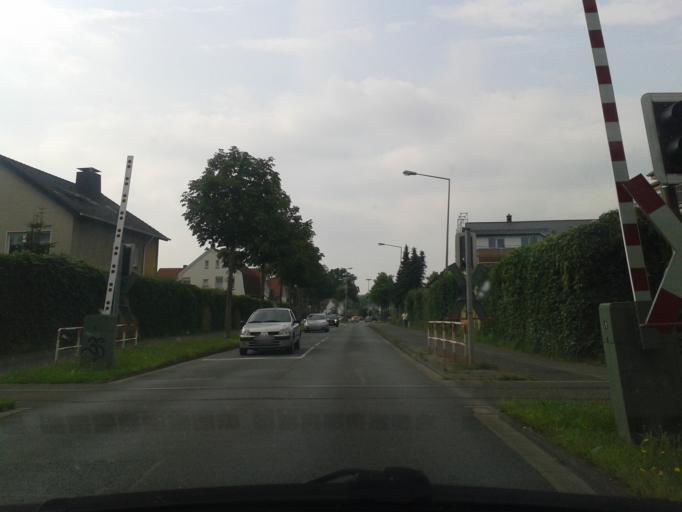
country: DE
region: North Rhine-Westphalia
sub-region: Regierungsbezirk Detmold
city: Paderborn
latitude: 51.7401
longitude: 8.7636
